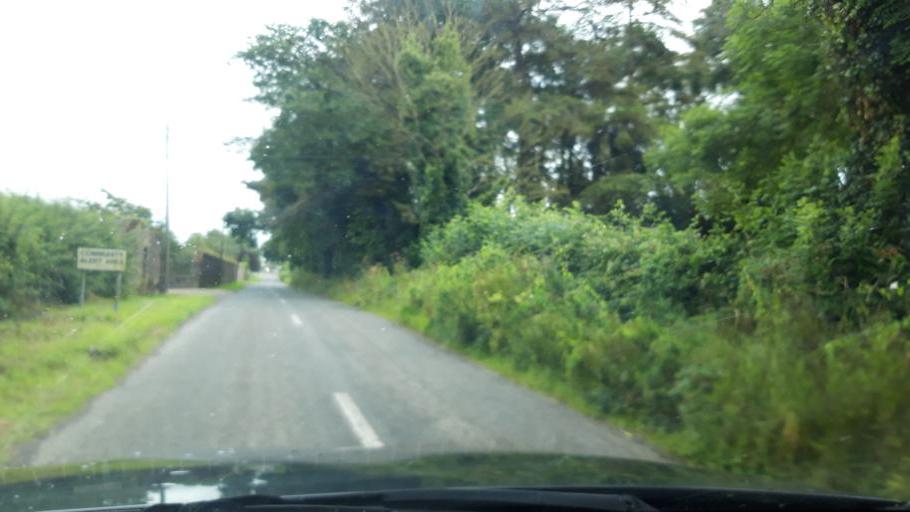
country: IE
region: Munster
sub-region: County Cork
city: Castlemartyr
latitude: 52.1354
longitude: -8.0237
